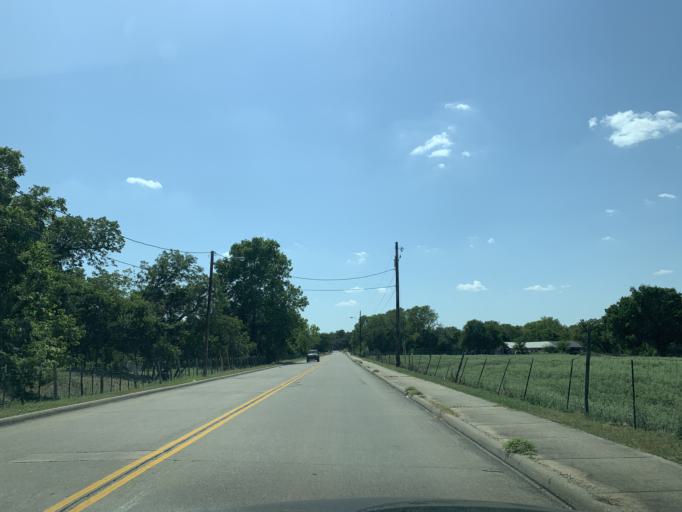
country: US
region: Texas
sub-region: Dallas County
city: Hutchins
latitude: 32.6797
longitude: -96.7896
